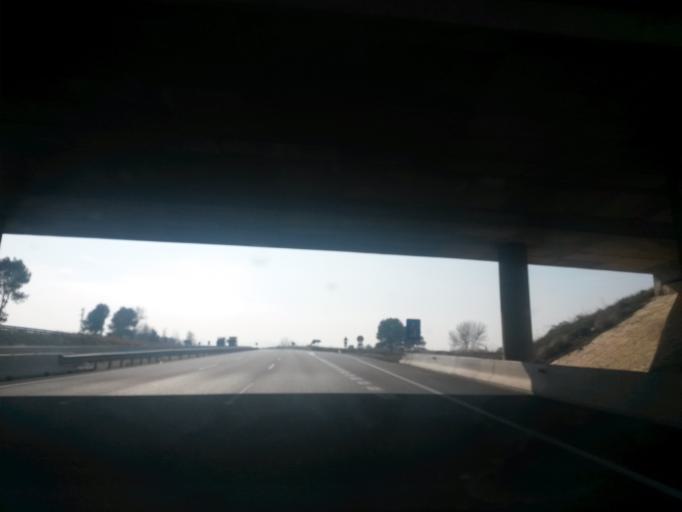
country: ES
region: Catalonia
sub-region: Provincia de Girona
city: Vilademuls
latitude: 42.1308
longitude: 2.9132
